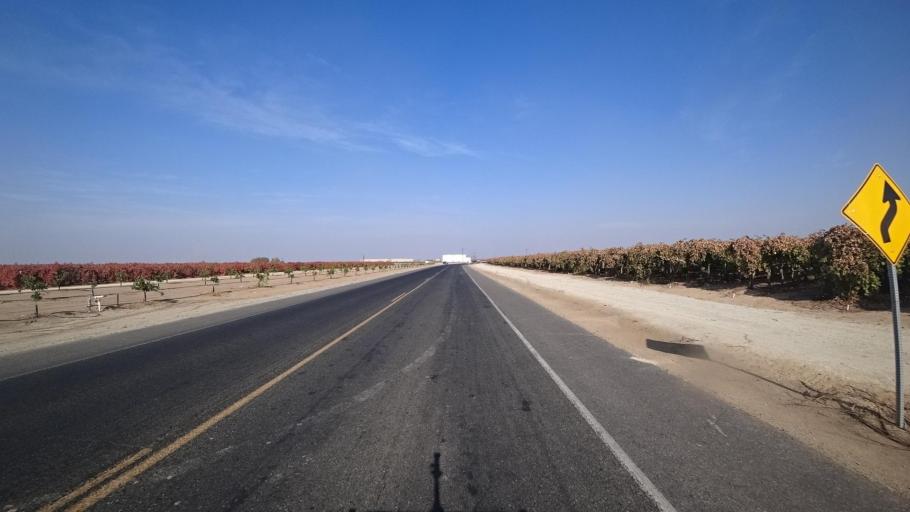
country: US
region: California
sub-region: Tulare County
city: Richgrove
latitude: 35.7376
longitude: -119.1475
